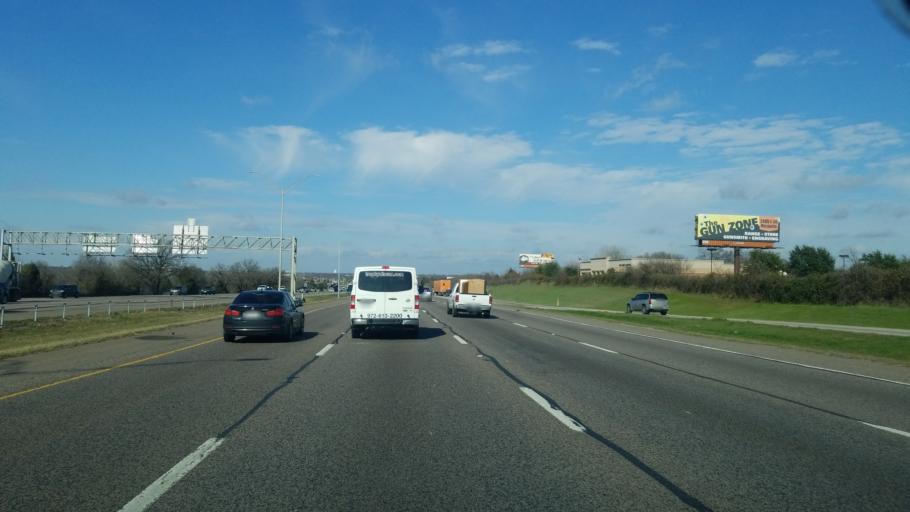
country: US
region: Texas
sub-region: Dallas County
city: Balch Springs
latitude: 32.7372
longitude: -96.6118
